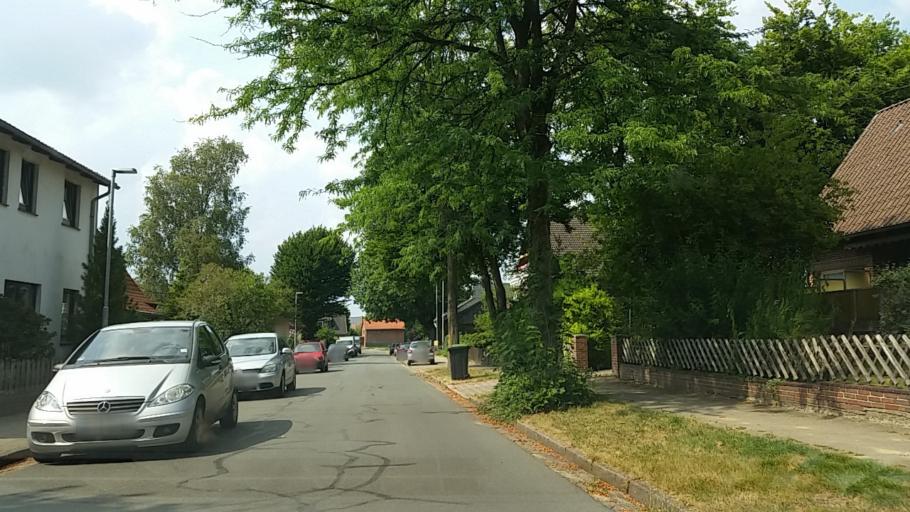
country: DE
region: Lower Saxony
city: Schneverdingen
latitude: 53.1251
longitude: 9.7875
